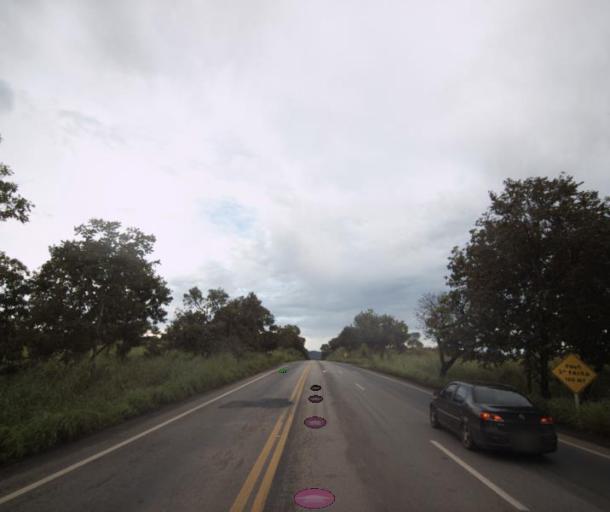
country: BR
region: Goias
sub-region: Porangatu
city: Porangatu
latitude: -13.7460
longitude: -49.0308
